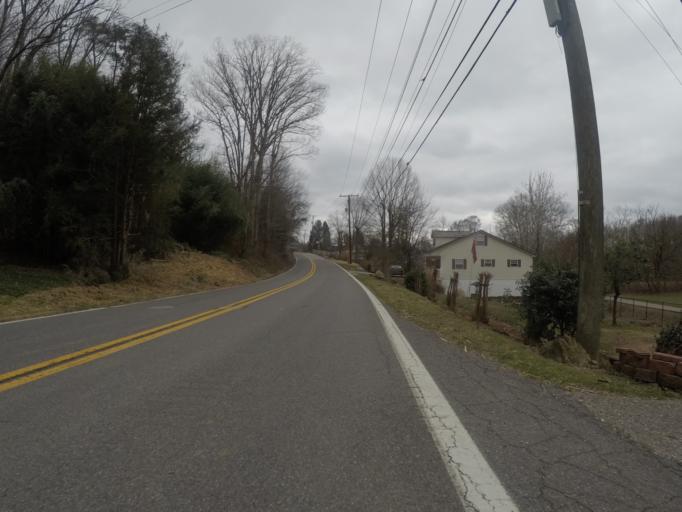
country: US
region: West Virginia
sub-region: Cabell County
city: Barboursville
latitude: 38.4240
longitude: -82.2915
